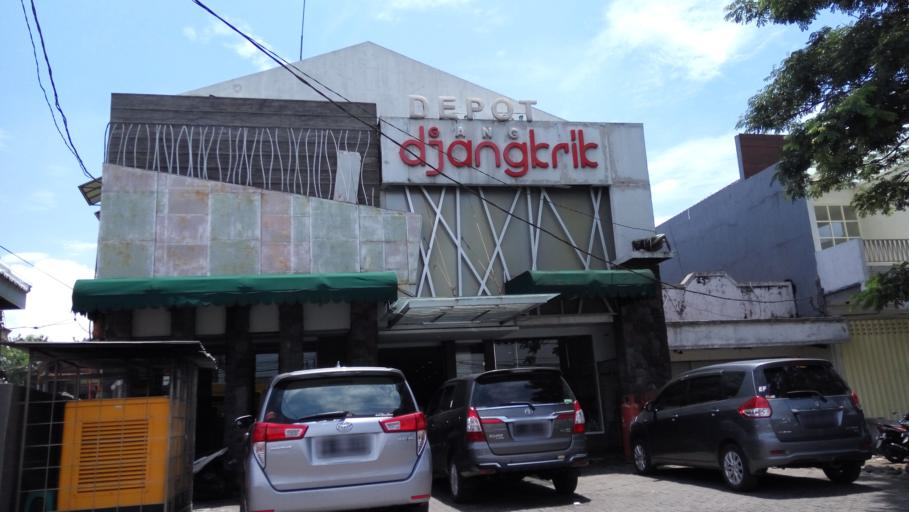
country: ID
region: East Java
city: Malang
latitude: -7.9565
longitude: 112.6381
